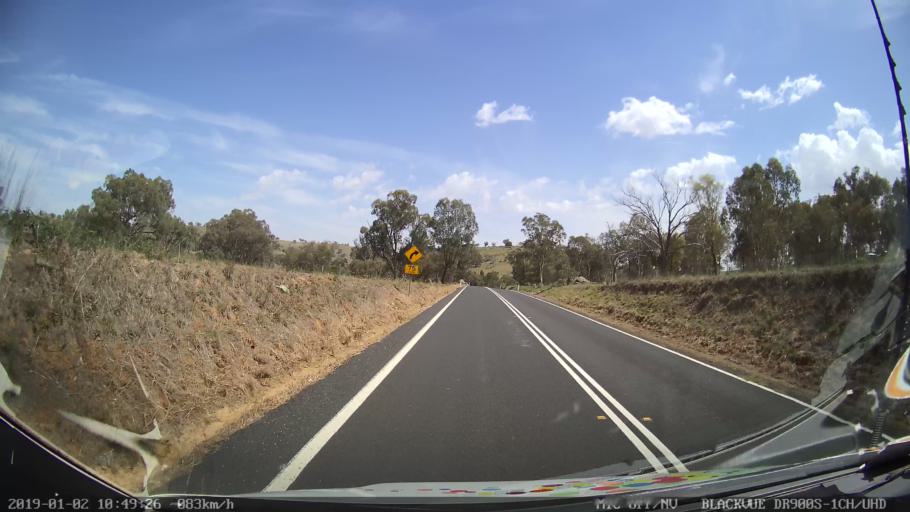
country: AU
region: New South Wales
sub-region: Cootamundra
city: Cootamundra
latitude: -34.7246
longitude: 148.2765
